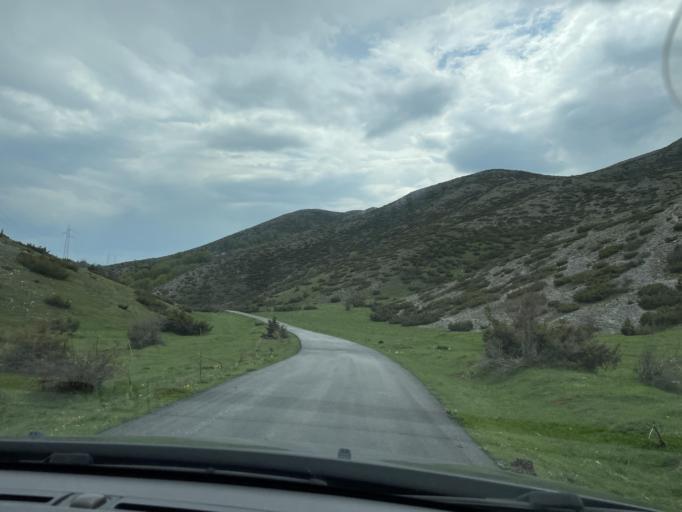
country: MK
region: Opstina Rostusa
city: Rostusha
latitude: 41.6144
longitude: 20.6815
